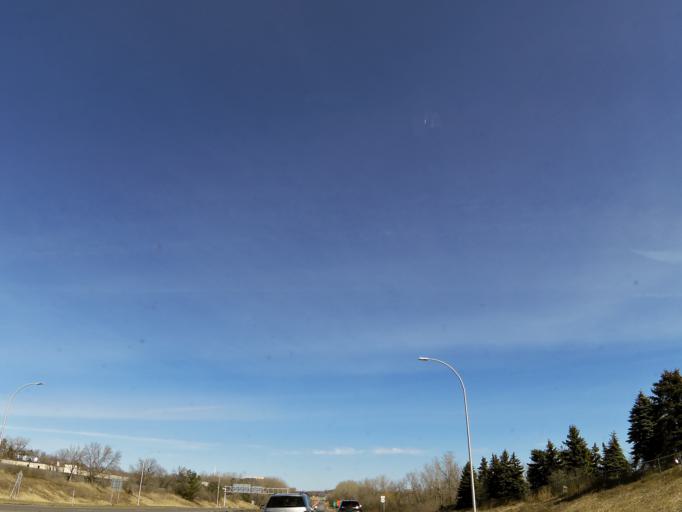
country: US
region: Minnesota
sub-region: Hennepin County
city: Eden Prairie
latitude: 44.8697
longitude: -93.4161
